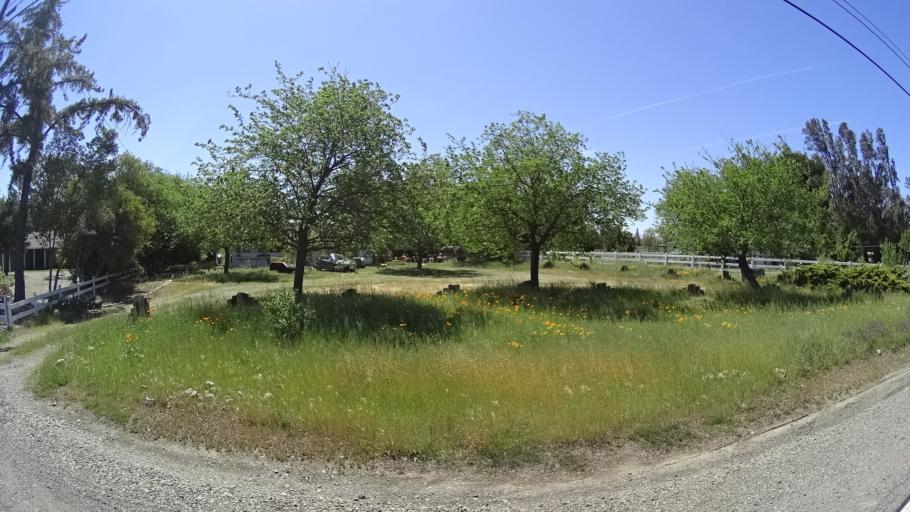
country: US
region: California
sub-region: Glenn County
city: Orland
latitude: 39.7321
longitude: -122.1585
